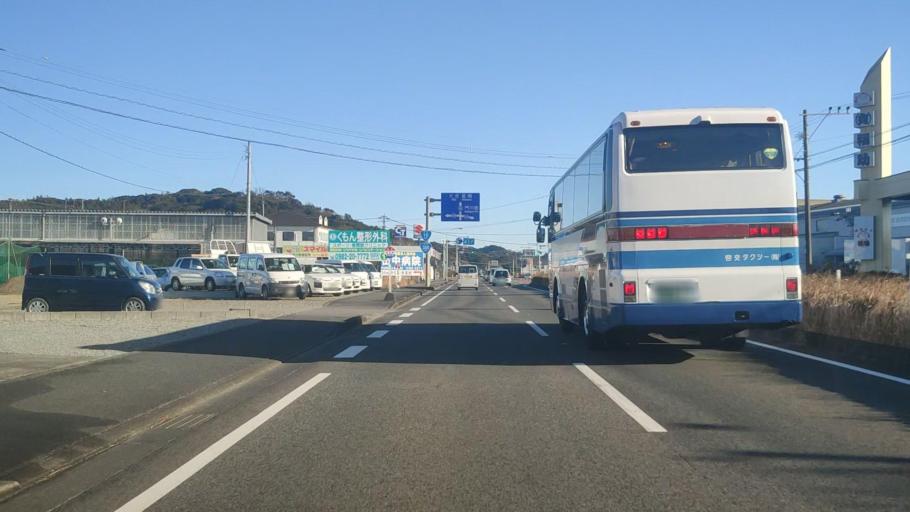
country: JP
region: Miyazaki
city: Nobeoka
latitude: 32.4781
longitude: 131.6552
